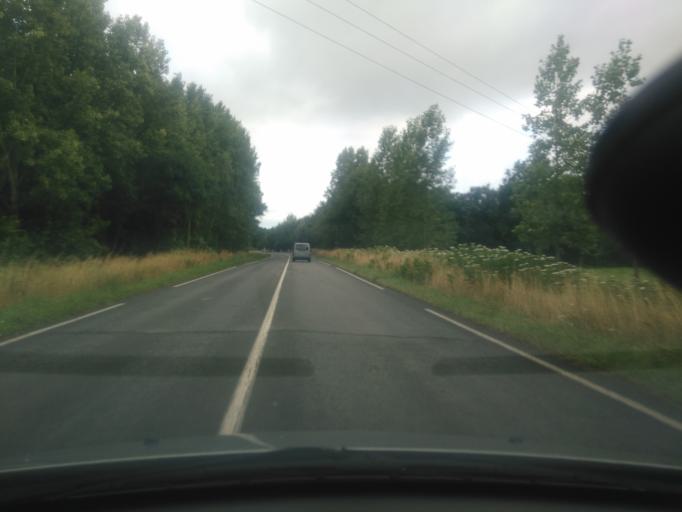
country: FR
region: Brittany
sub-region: Departement des Cotes-d'Armor
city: Lanvallay
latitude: 48.4474
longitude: -1.9933
